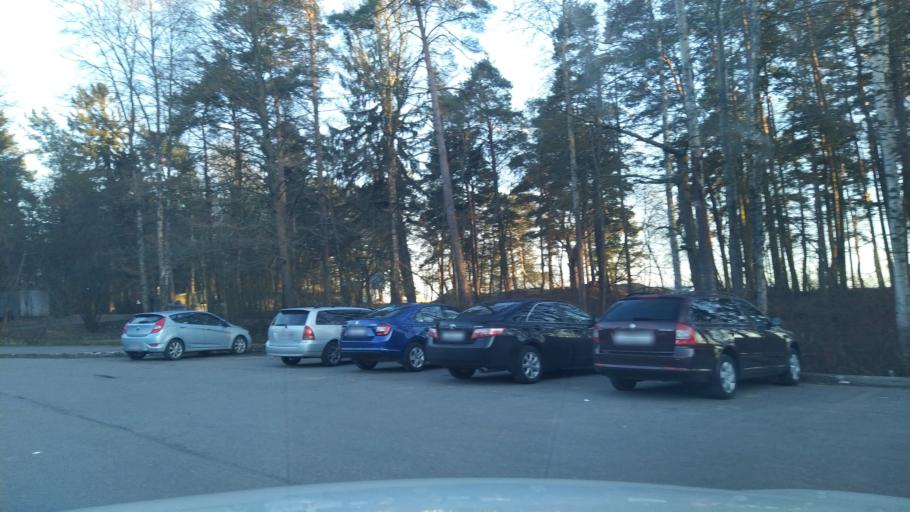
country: RU
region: St.-Petersburg
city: Solnechnoye
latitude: 60.1461
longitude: 29.9270
